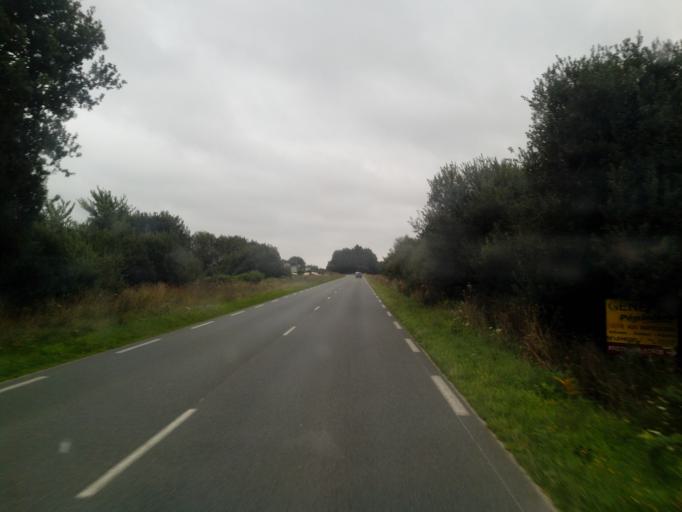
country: FR
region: Brittany
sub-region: Departement des Cotes-d'Armor
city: Plehedel
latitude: 48.7289
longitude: -3.0266
